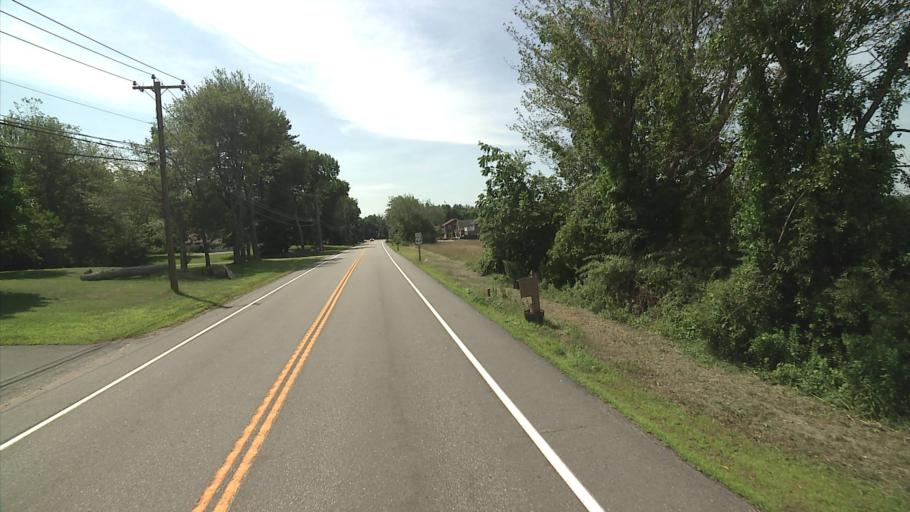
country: US
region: Connecticut
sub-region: Tolland County
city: Coventry Lake
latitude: 41.8005
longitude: -72.3939
